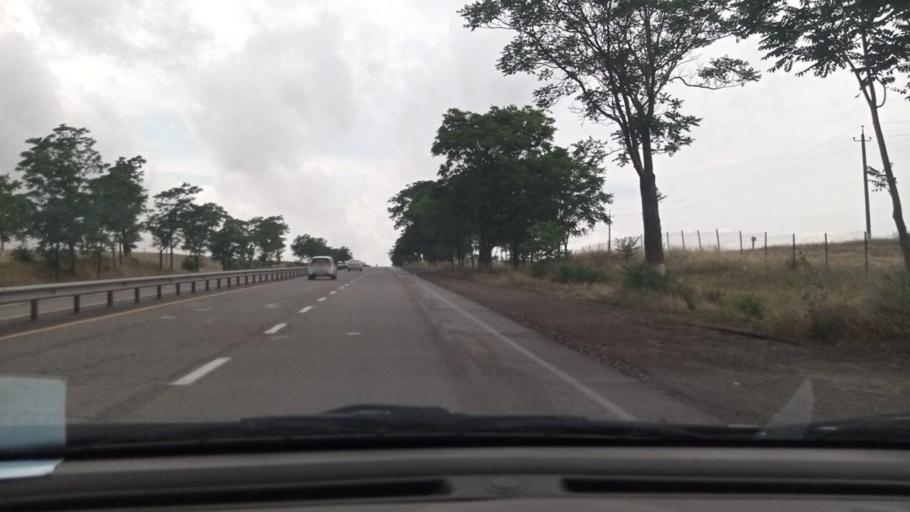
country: UZ
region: Toshkent
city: Ohangaron
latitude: 40.9581
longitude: 69.5615
